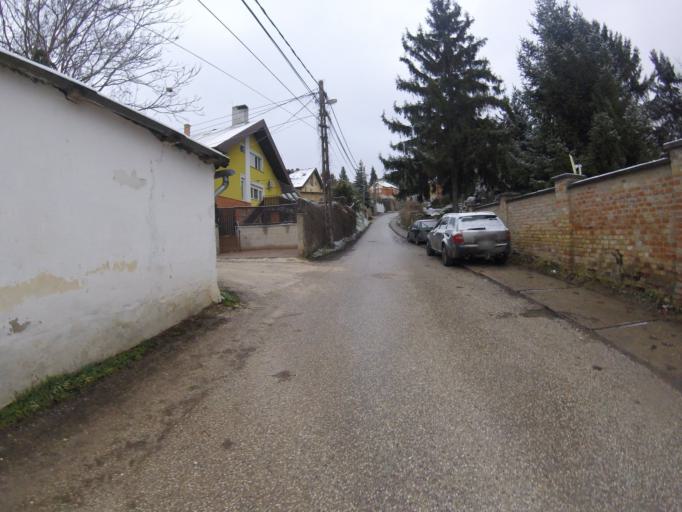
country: HU
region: Komarom-Esztergom
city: Esztergom
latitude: 47.7886
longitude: 18.7465
